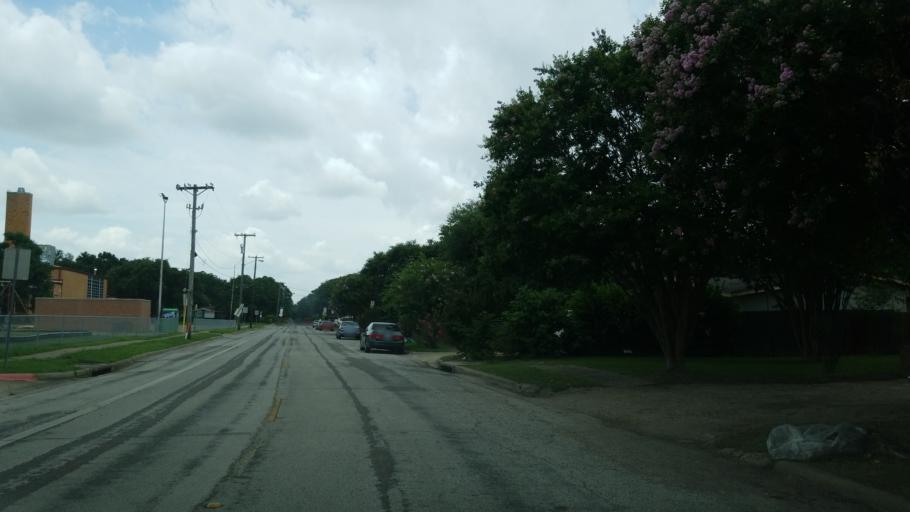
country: US
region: Texas
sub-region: Dallas County
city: Farmers Branch
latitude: 32.8894
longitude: -96.8760
